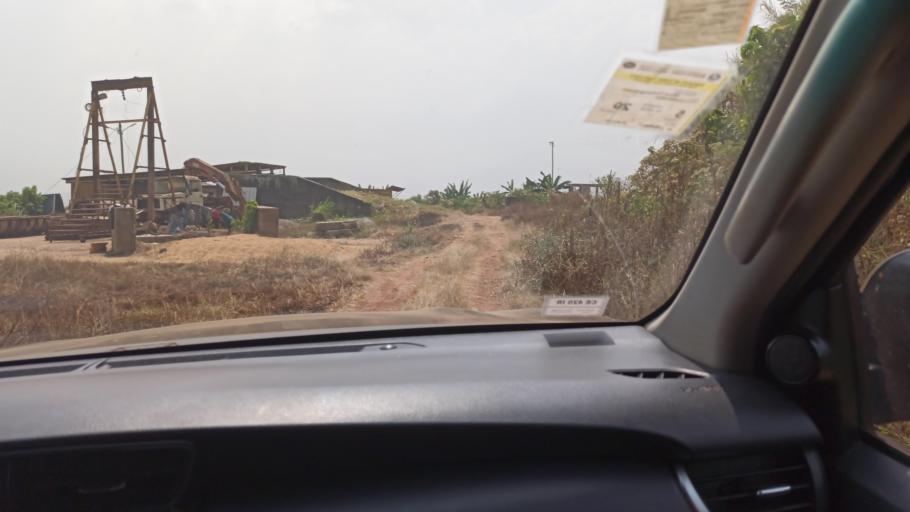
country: CM
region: Centre
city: Yaounde
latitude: 3.8881
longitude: 11.4867
